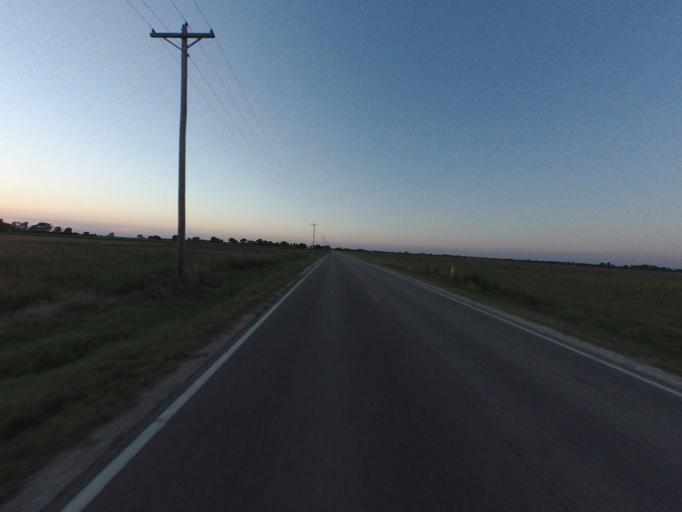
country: US
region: Kansas
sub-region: Rice County
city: Sterling
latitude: 38.1815
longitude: -98.2069
